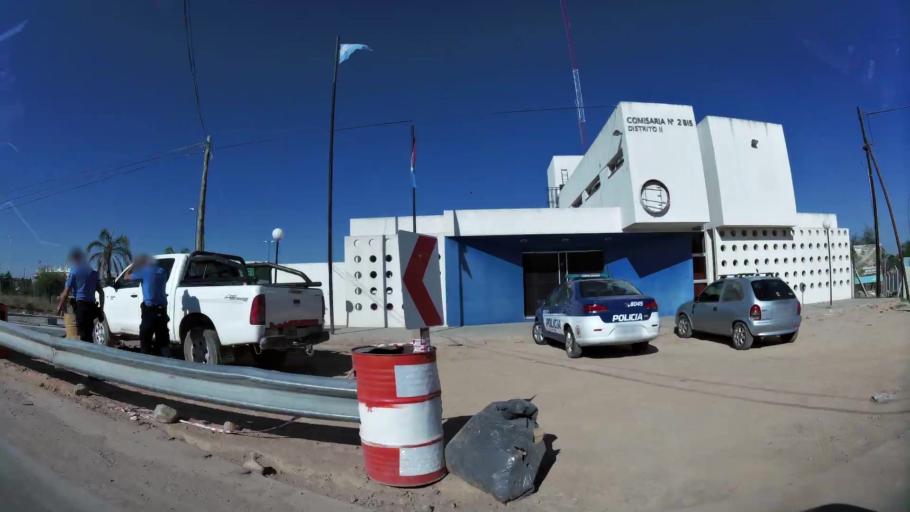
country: AR
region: Cordoba
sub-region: Departamento de Capital
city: Cordoba
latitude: -31.3725
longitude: -64.2503
